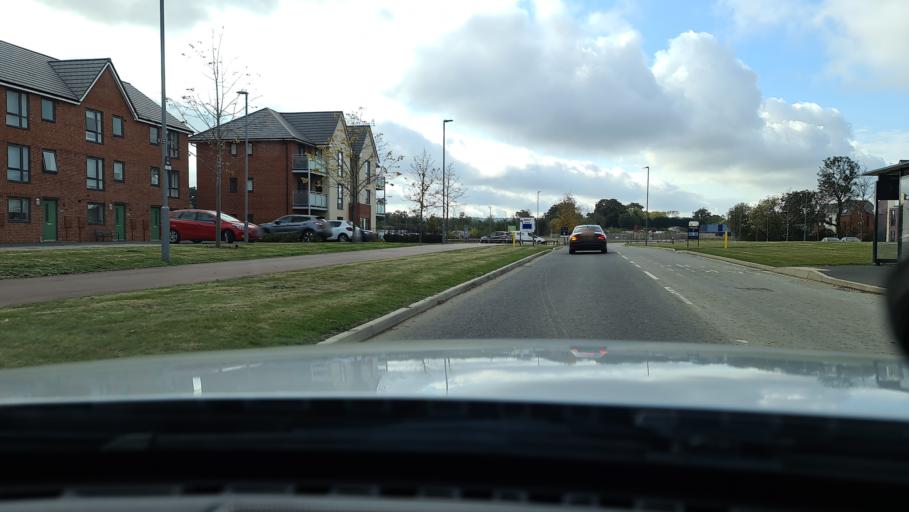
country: GB
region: England
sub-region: Milton Keynes
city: Woburn Sands
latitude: 52.0358
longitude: -0.6505
